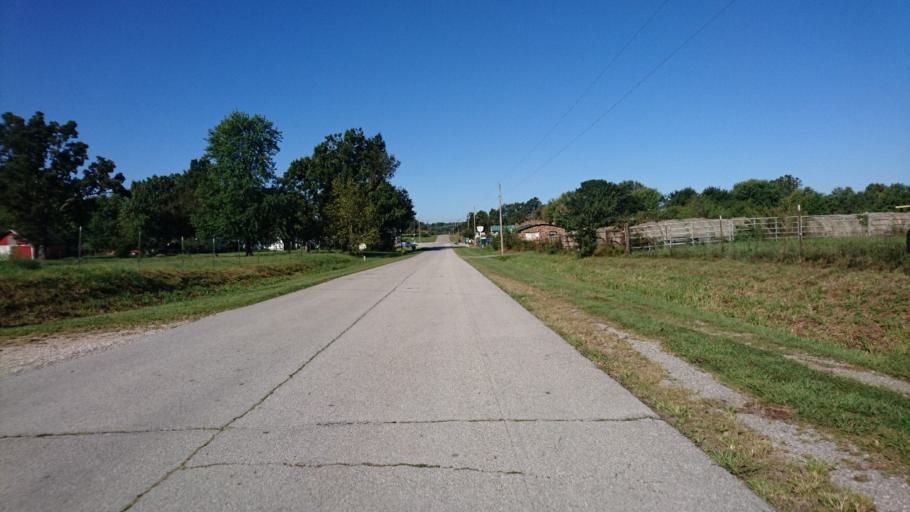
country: US
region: Missouri
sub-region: Greene County
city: Ash Grove
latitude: 37.1943
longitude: -93.6774
